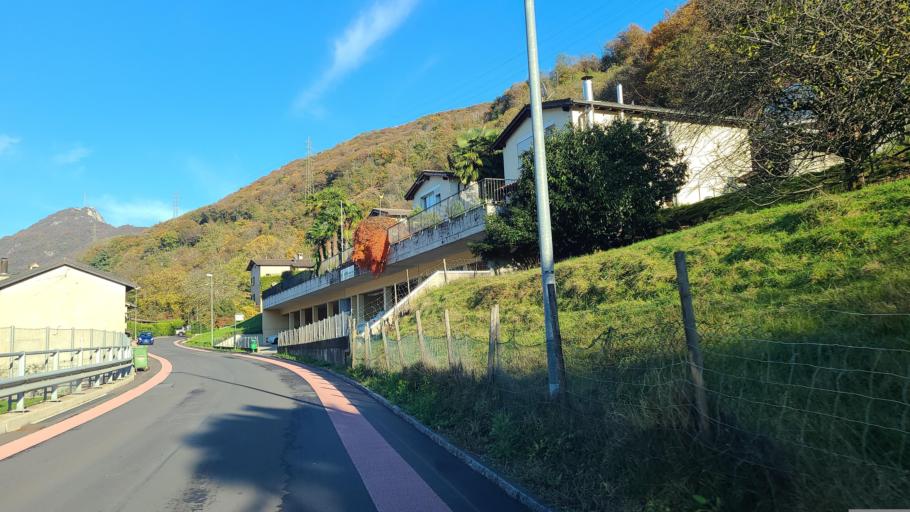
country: CH
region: Ticino
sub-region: Lugano District
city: Montagnola
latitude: 45.9554
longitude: 8.9190
